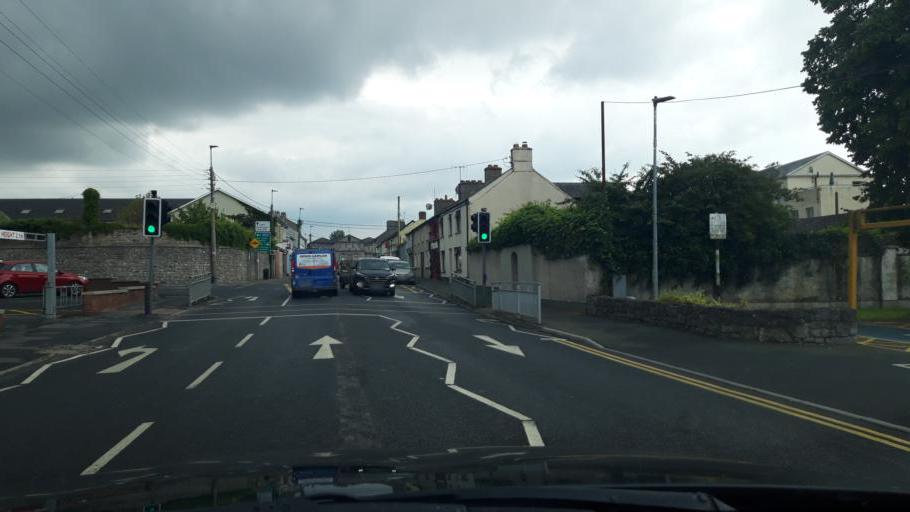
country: IE
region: Leinster
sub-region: Kildare
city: Athy
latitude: 52.9937
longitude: -6.9840
